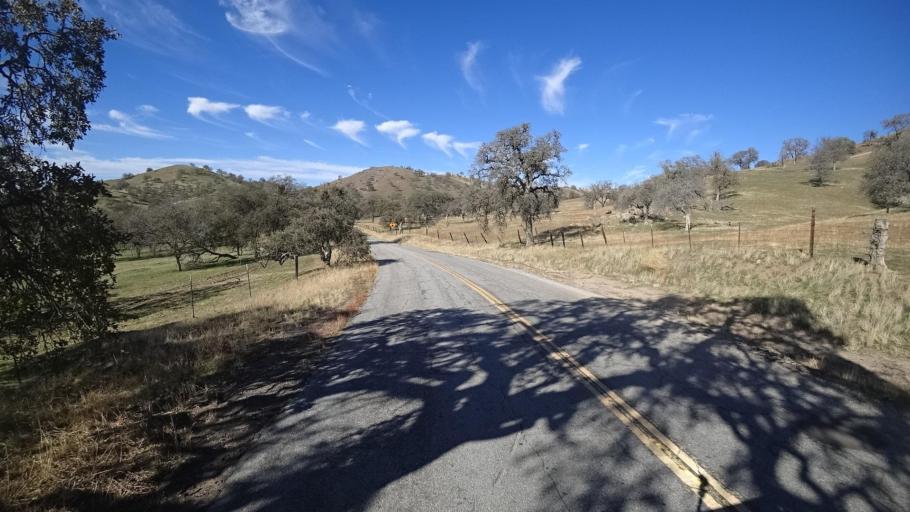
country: US
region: California
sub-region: Kern County
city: Alta Sierra
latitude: 35.6299
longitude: -118.7982
